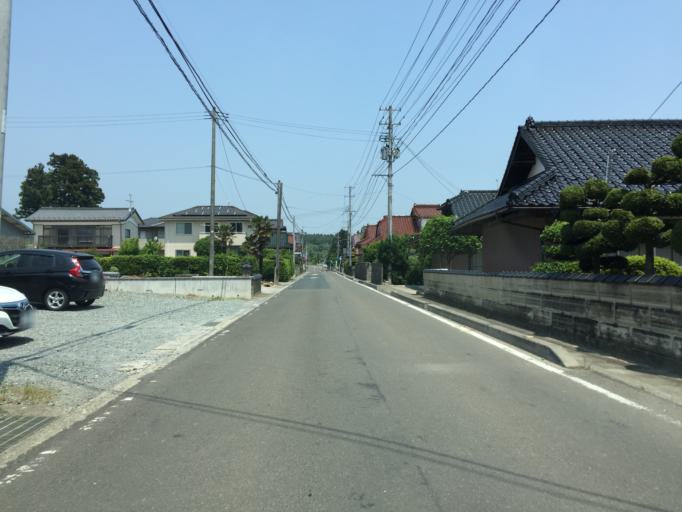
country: JP
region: Miyagi
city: Marumori
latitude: 37.8290
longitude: 140.8957
